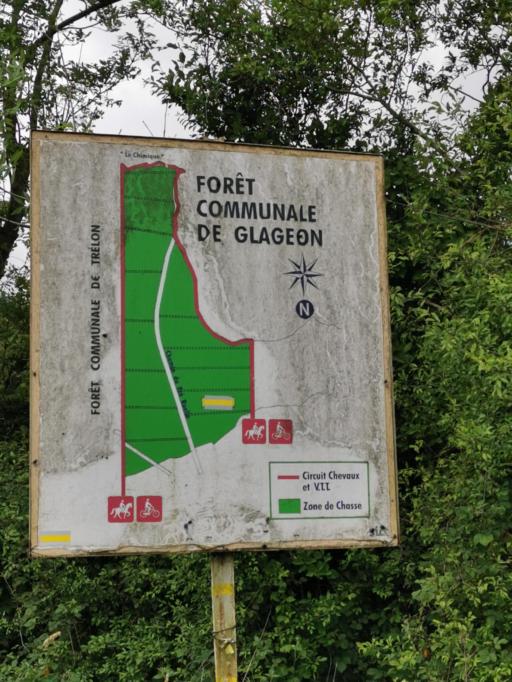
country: FR
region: Nord-Pas-de-Calais
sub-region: Departement du Nord
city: Trelon
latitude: 50.0426
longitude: 4.0836
